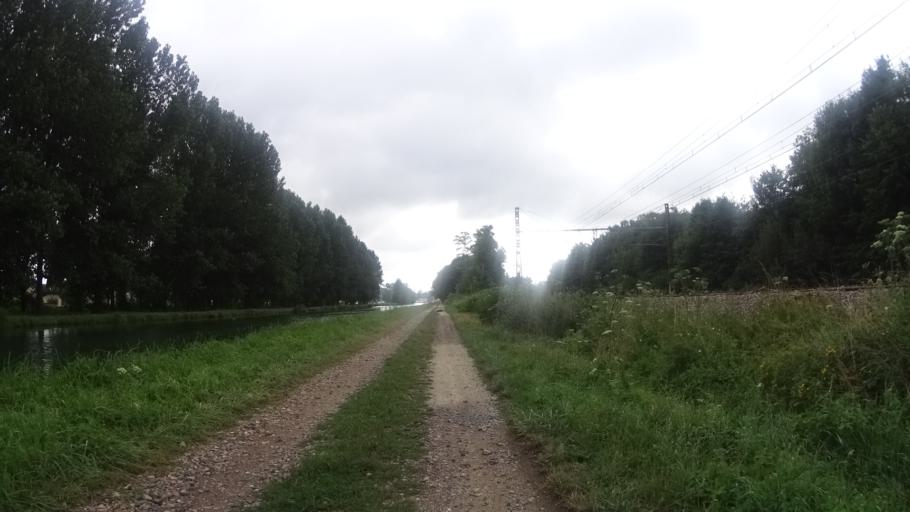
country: FR
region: Bourgogne
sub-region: Departement de l'Yonne
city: Brienon-sur-Armancon
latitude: 47.9890
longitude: 3.6020
